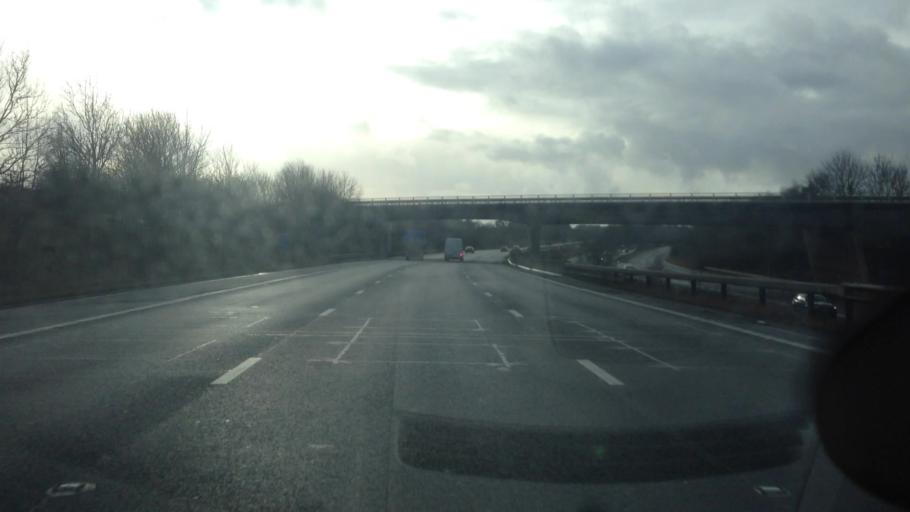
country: GB
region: England
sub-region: City and Borough of Wakefield
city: Crigglestone
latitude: 53.6306
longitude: -1.5402
